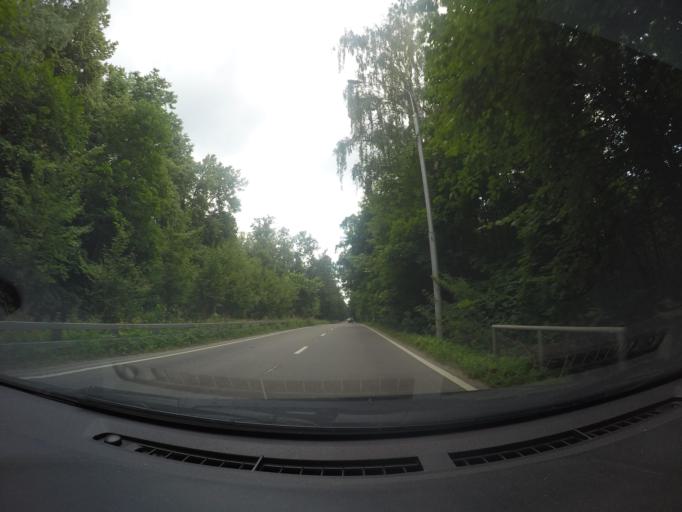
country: RU
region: Moscow
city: Sokol'niki
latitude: 55.8131
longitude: 37.6739
